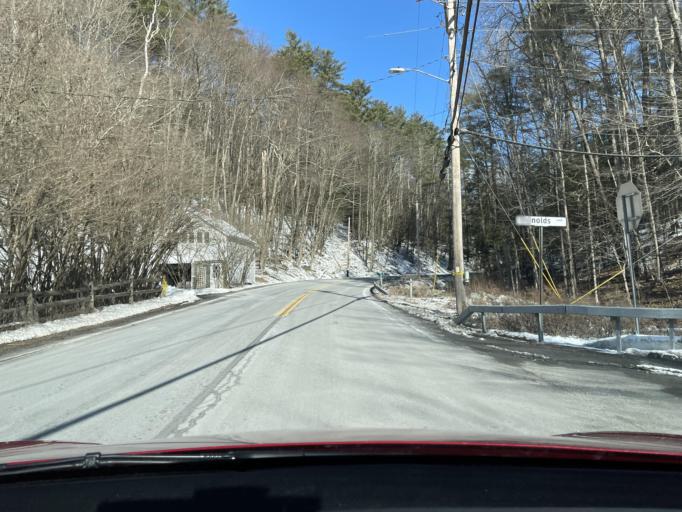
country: US
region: New York
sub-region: Ulster County
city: Woodstock
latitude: 42.0603
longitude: -74.1603
